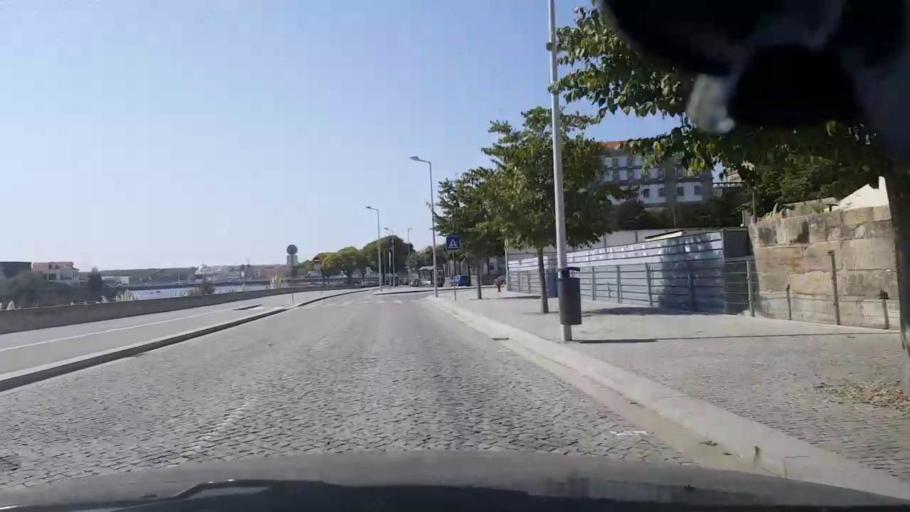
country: PT
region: Porto
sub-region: Vila do Conde
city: Vila do Conde
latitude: 41.3521
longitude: -8.7359
